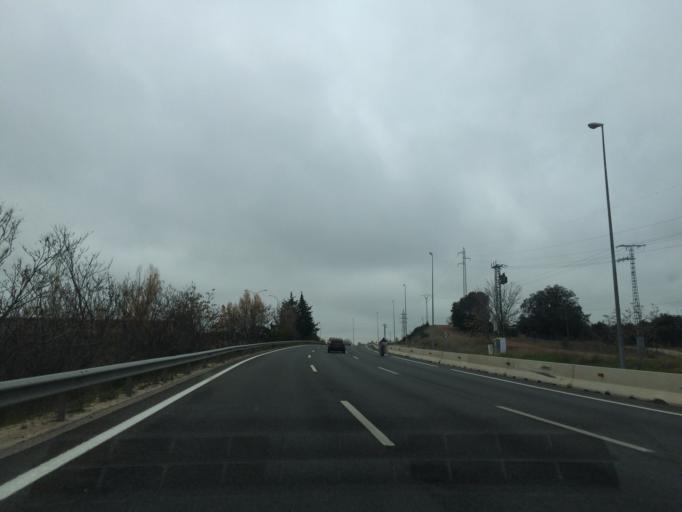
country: ES
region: Madrid
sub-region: Provincia de Madrid
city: Tres Cantos
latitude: 40.5679
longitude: -3.7120
